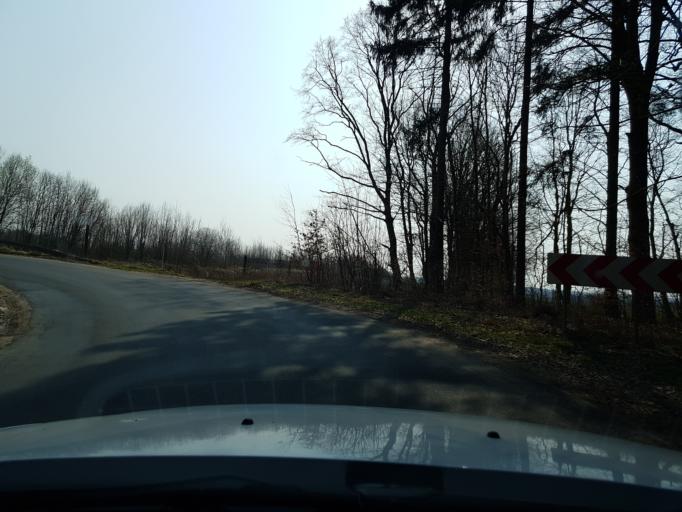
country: PL
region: West Pomeranian Voivodeship
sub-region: Powiat koszalinski
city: Sianow
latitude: 54.2568
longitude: 16.3117
